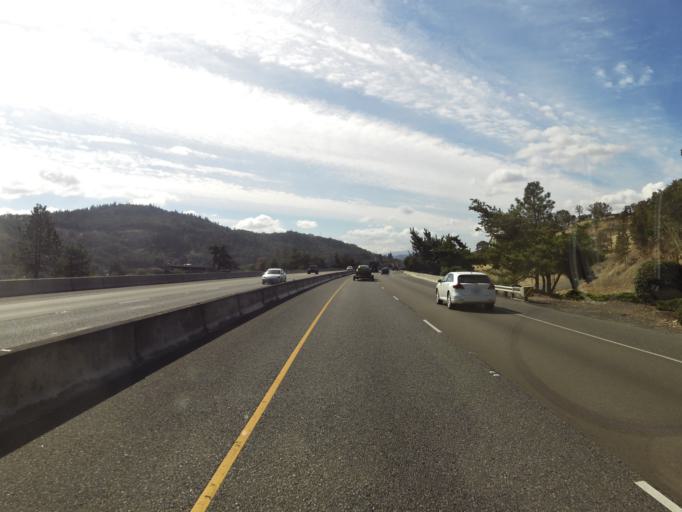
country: US
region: Oregon
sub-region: Douglas County
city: Roseburg
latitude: 43.2000
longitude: -123.3592
